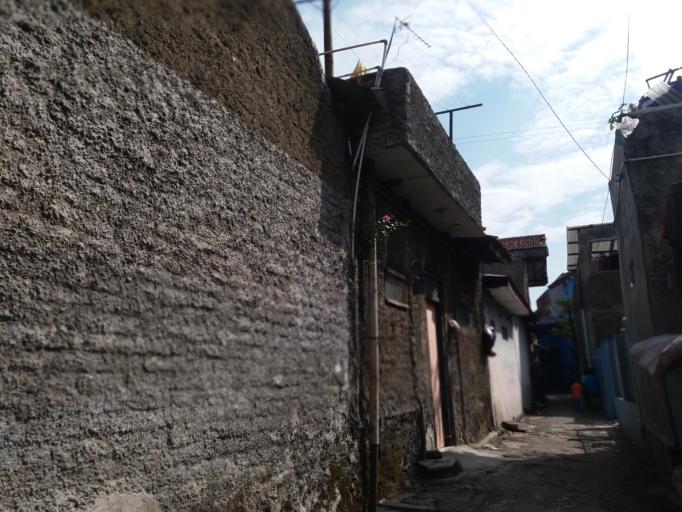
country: ID
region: West Java
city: Bandung
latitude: -6.9222
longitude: 107.6549
